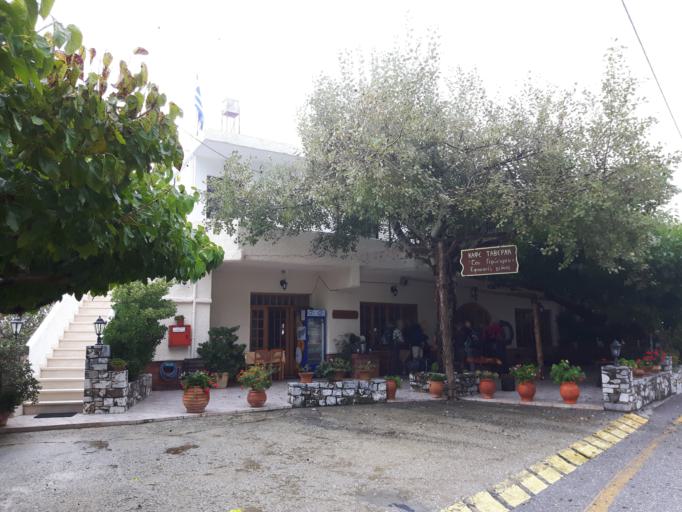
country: GR
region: Crete
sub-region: Nomos Chanias
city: Chora Sfakion
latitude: 35.2936
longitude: 24.1764
